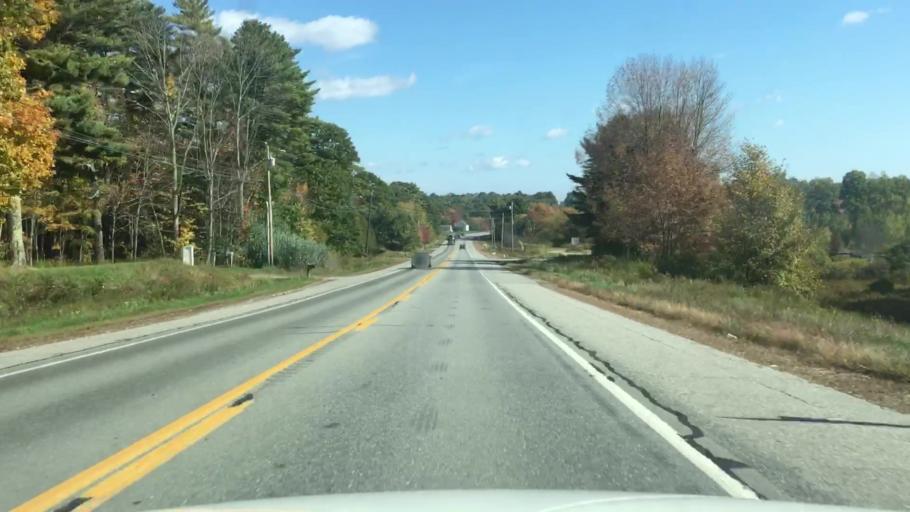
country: US
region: Maine
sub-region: Knox County
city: Warren
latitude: 44.1196
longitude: -69.2929
